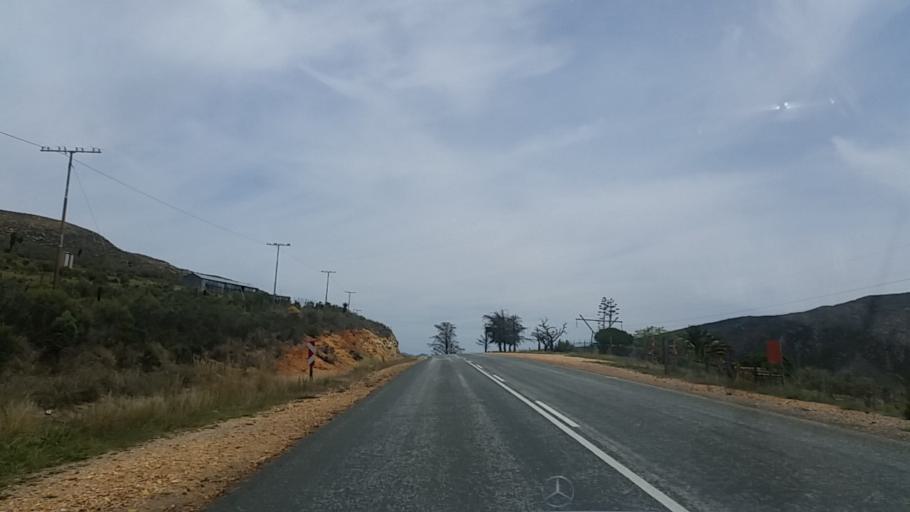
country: ZA
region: Western Cape
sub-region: Eden District Municipality
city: Knysna
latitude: -33.7443
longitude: 22.9930
